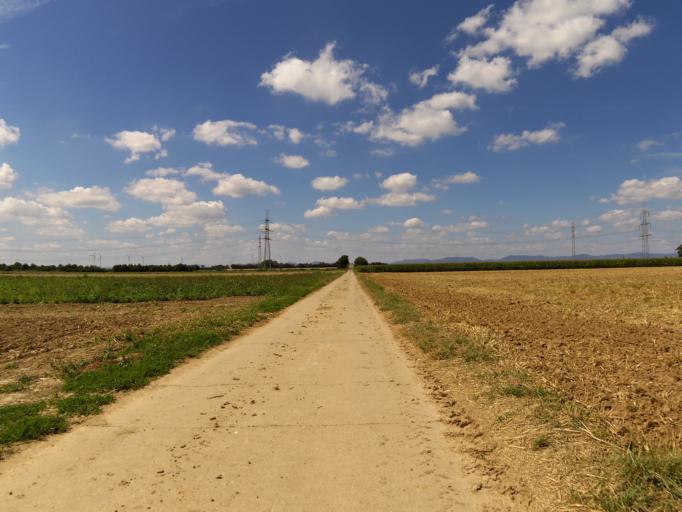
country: DE
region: Rheinland-Pfalz
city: Hordt
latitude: 49.1729
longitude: 8.3108
